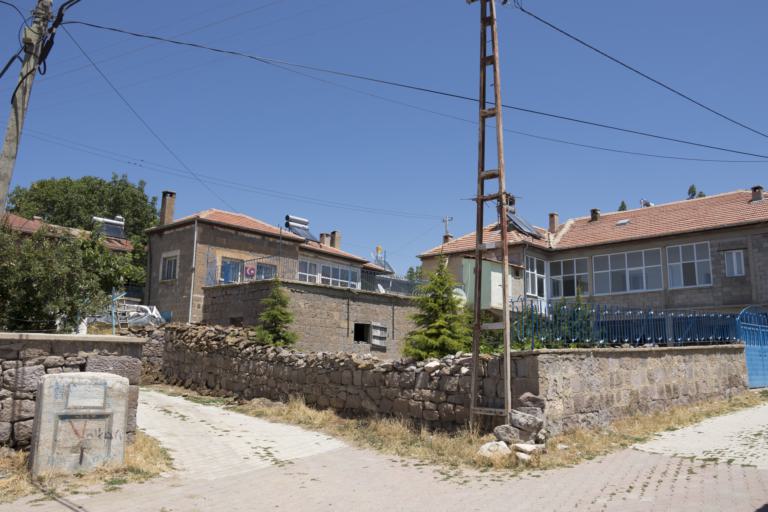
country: TR
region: Kayseri
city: Toklar
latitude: 38.4076
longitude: 36.0825
